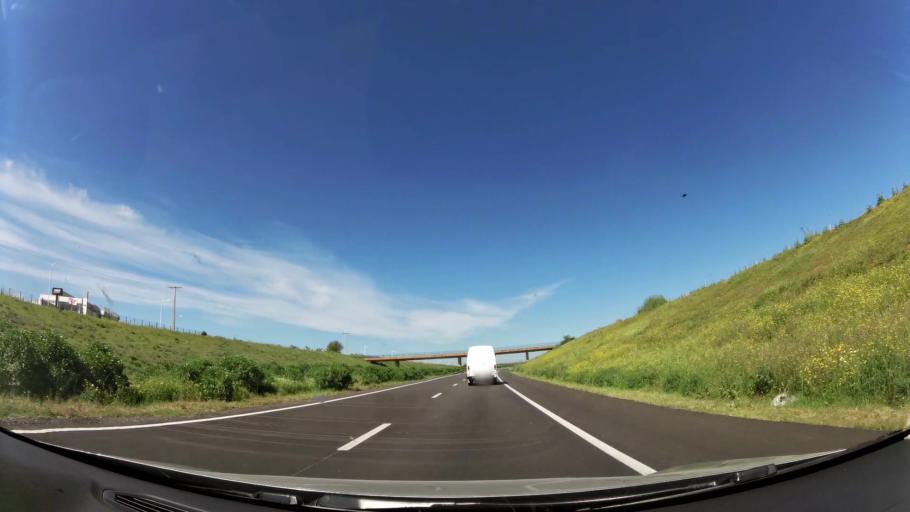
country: MA
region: Meknes-Tafilalet
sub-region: Meknes
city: Meknes
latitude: 33.8341
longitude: -5.4696
